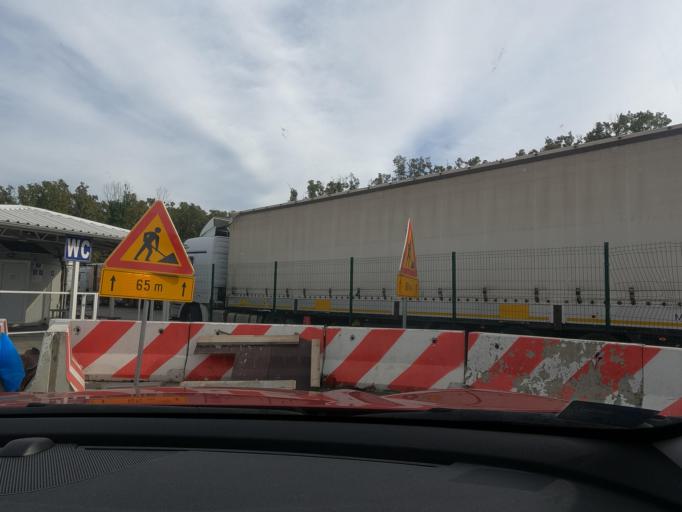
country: HR
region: Vukovarsko-Srijemska
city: Nijemci
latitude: 45.0468
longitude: 19.1081
